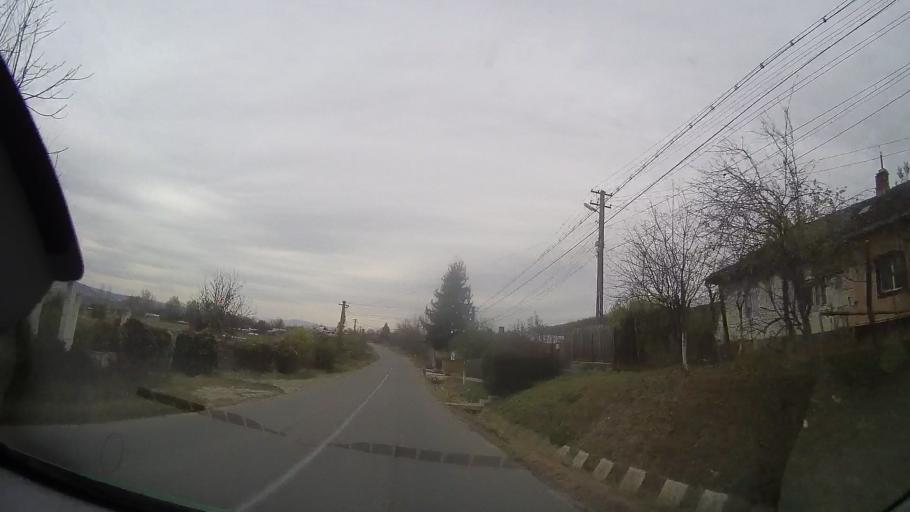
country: RO
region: Prahova
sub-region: Comuna Iordachianu
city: Iordacheanu
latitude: 45.0258
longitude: 26.2387
